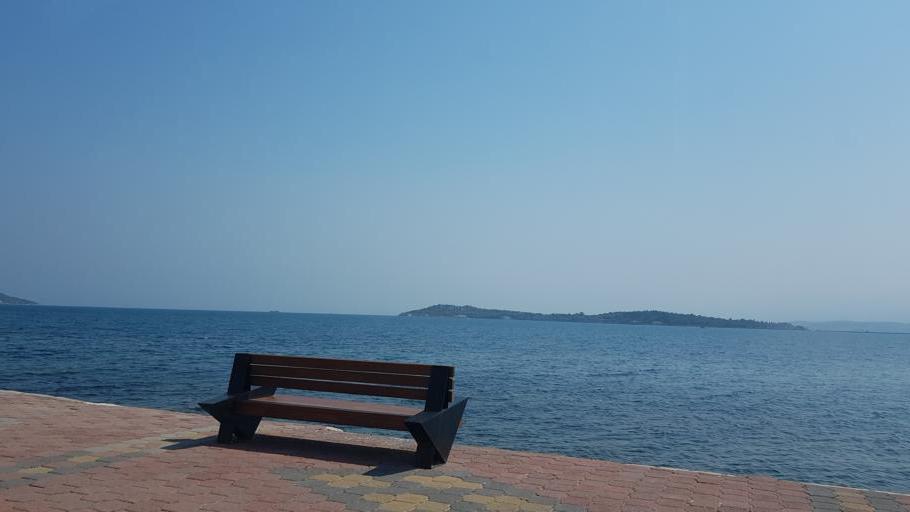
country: TR
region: Izmir
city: Urla
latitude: 38.3688
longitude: 26.7642
